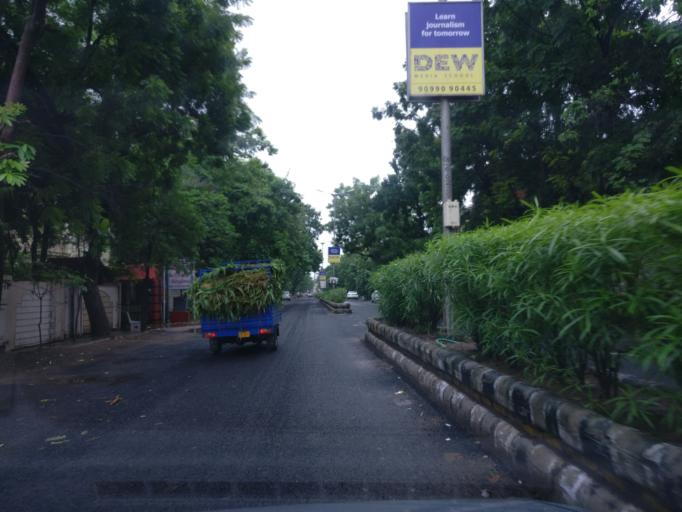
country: IN
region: Gujarat
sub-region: Ahmadabad
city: Sarkhej
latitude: 23.0202
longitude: 72.5075
